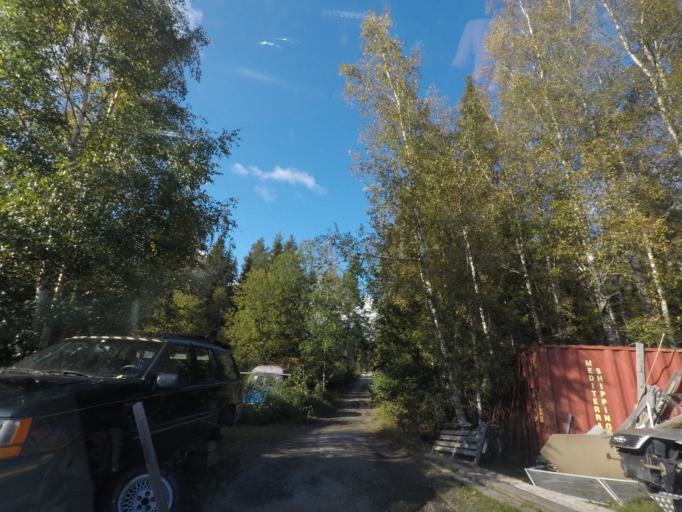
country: SE
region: Vaestmanland
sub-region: Skinnskattebergs Kommun
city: Skinnskatteberg
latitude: 59.8302
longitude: 15.5504
